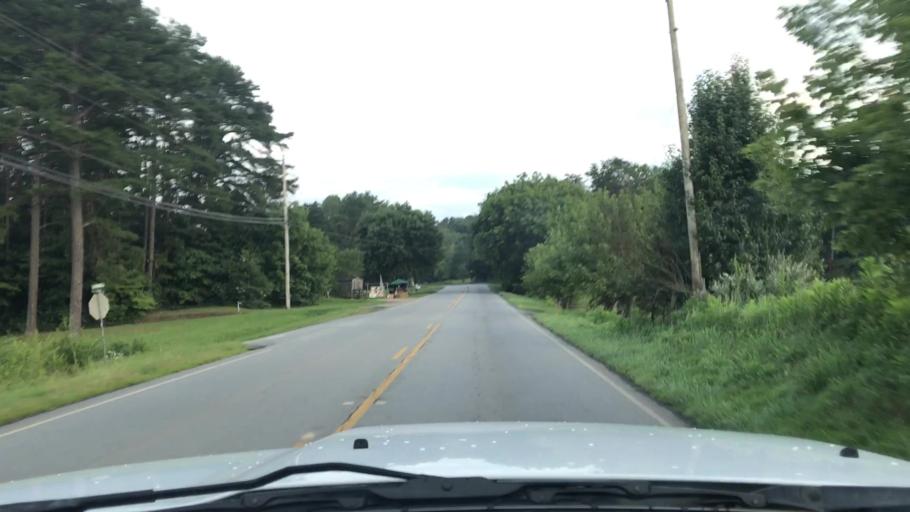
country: US
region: Georgia
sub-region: Fannin County
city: Blue Ridge
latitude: 34.9002
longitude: -84.2651
